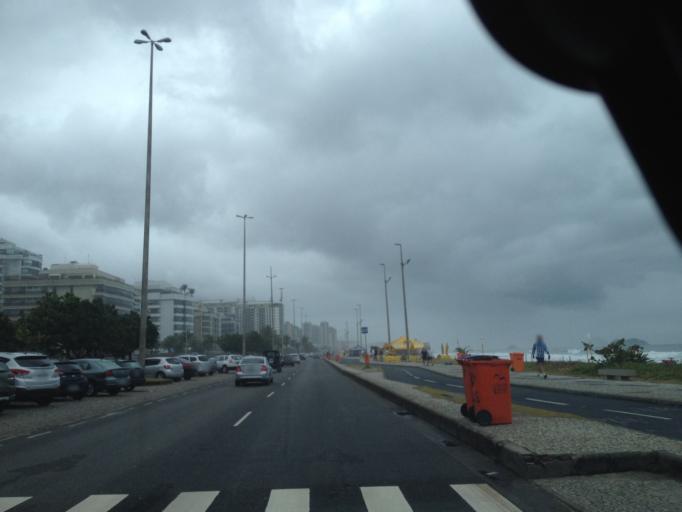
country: BR
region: Rio de Janeiro
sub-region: Rio De Janeiro
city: Rio de Janeiro
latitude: -23.0104
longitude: -43.3514
